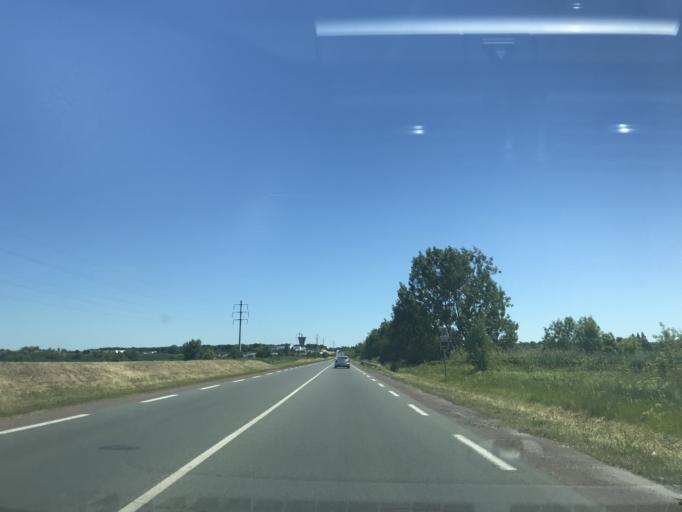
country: FR
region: Poitou-Charentes
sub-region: Departement de la Charente-Maritime
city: Royan
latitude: 45.6352
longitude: -1.0148
